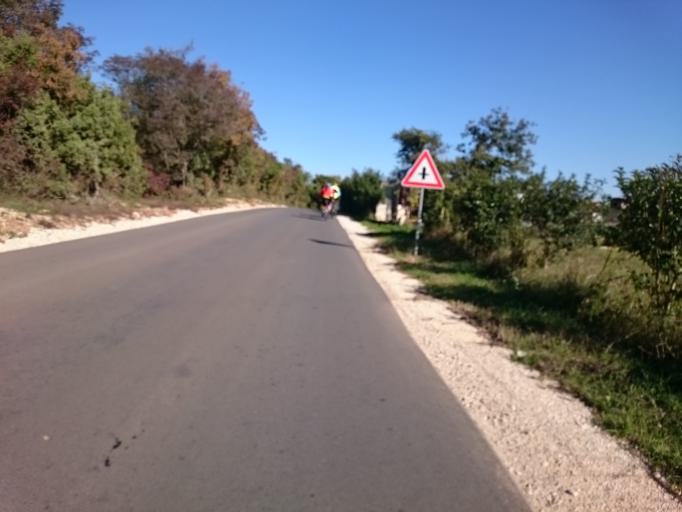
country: HR
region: Istarska
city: Umag
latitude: 45.4588
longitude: 13.5403
